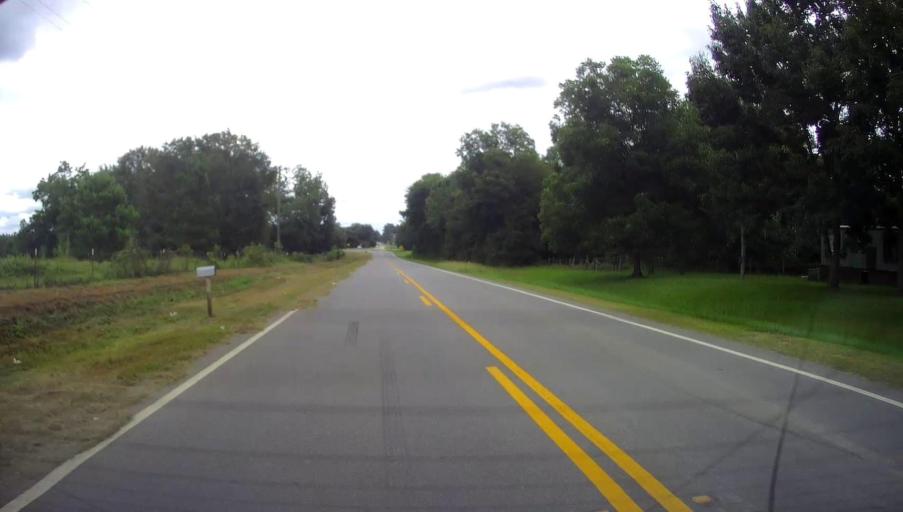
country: US
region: Georgia
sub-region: Macon County
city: Oglethorpe
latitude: 32.2670
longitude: -84.0886
